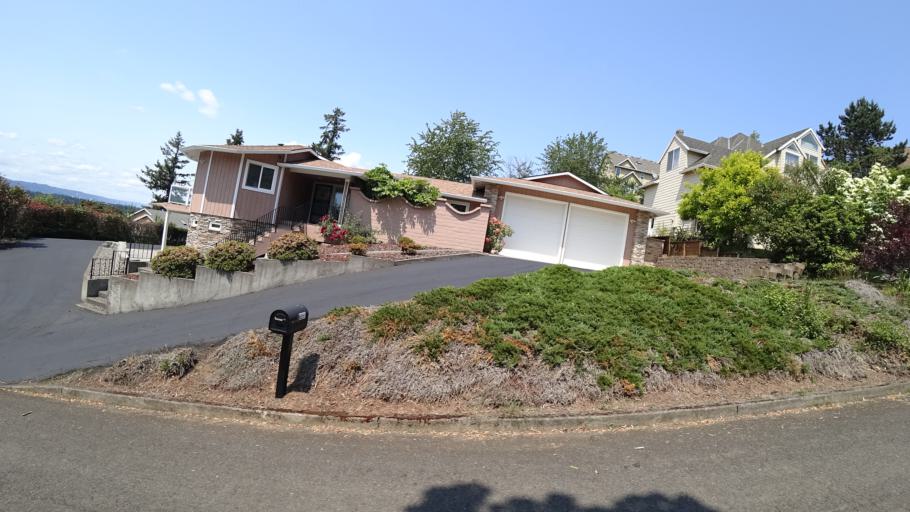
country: US
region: Oregon
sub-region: Multnomah County
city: Lents
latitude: 45.4537
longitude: -122.5674
